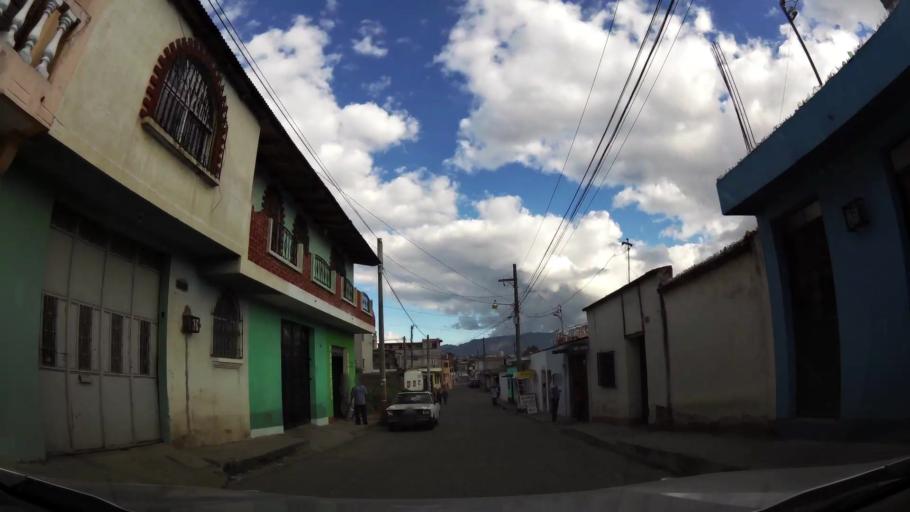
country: GT
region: Quetzaltenango
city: Quetzaltenango
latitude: 14.8519
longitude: -91.5188
